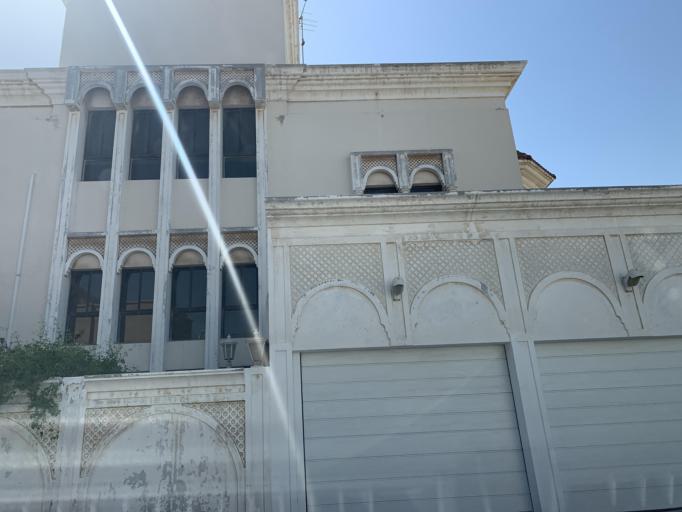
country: BH
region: Manama
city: Manama
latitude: 26.2142
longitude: 50.5806
